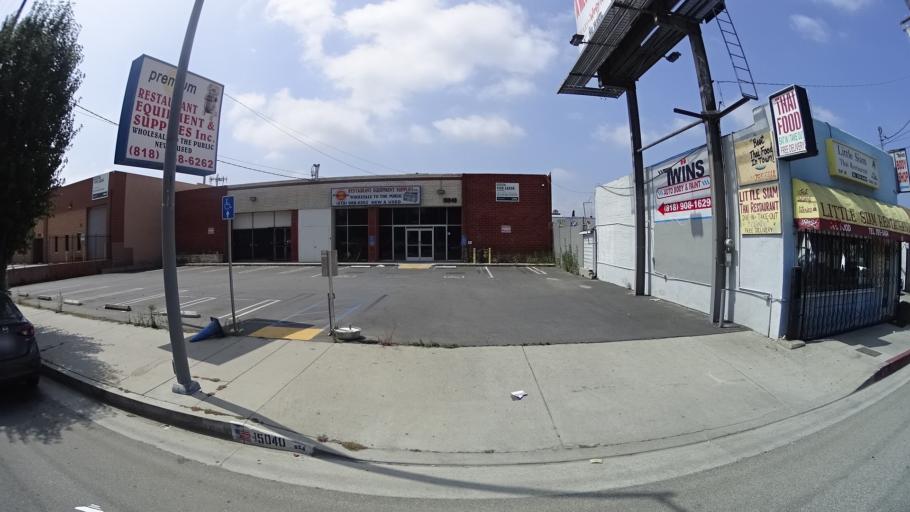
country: US
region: California
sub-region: Los Angeles County
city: Van Nuys
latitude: 34.1794
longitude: -118.4611
